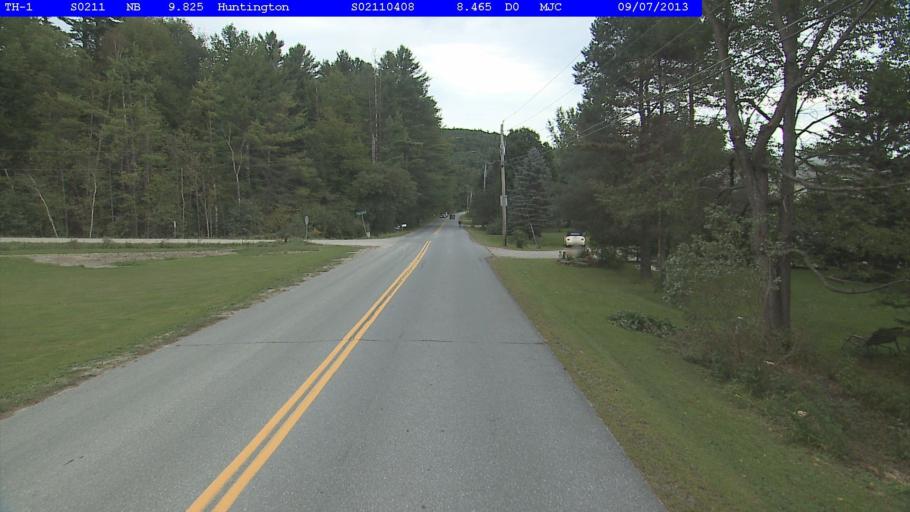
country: US
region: Vermont
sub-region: Chittenden County
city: Hinesburg
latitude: 44.3373
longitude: -72.9974
